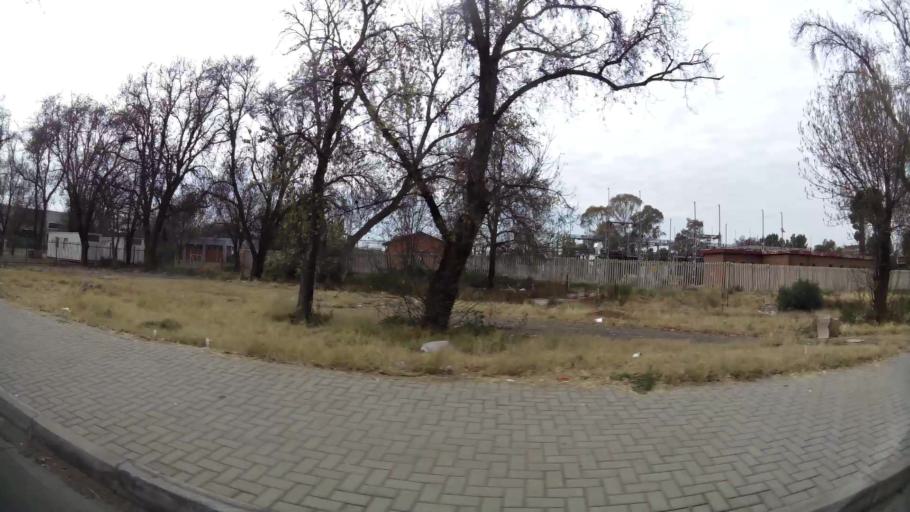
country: ZA
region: Orange Free State
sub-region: Mangaung Metropolitan Municipality
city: Bloemfontein
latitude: -29.1179
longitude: 26.2003
